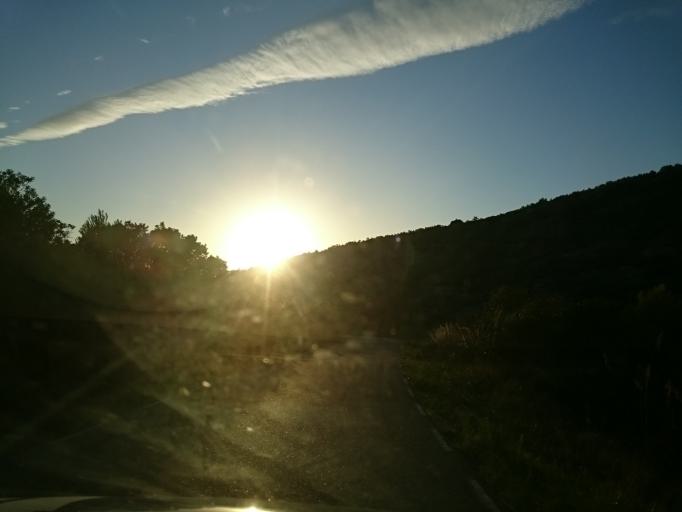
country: ES
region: Catalonia
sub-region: Provincia de Barcelona
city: Olivella
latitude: 41.3046
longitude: 1.8278
